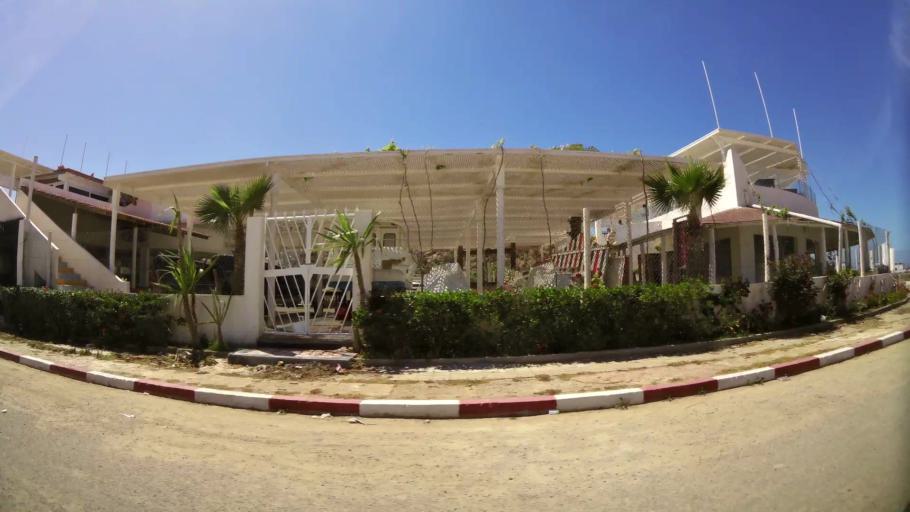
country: MA
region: Oriental
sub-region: Berkane-Taourirt
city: Madagh
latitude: 35.1424
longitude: -2.4222
